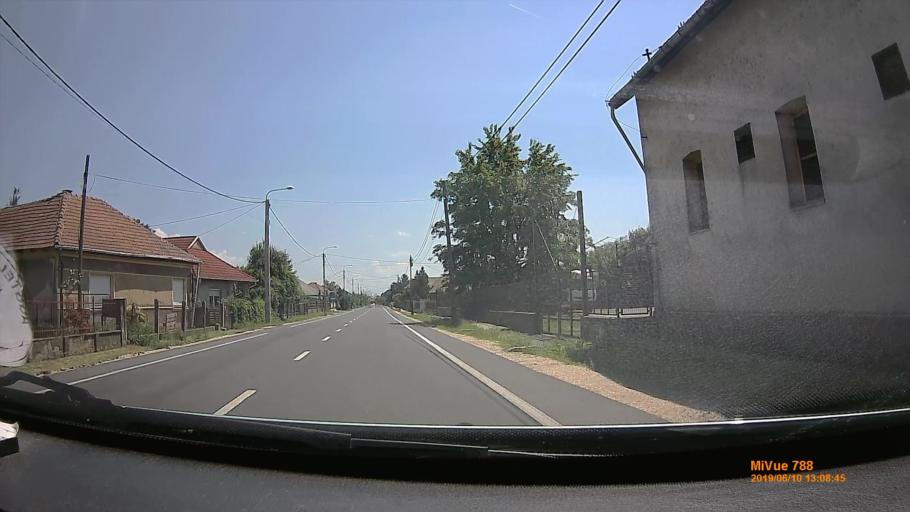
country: HU
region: Borsod-Abauj-Zemplen
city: Hernadnemeti
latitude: 48.0779
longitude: 20.9740
